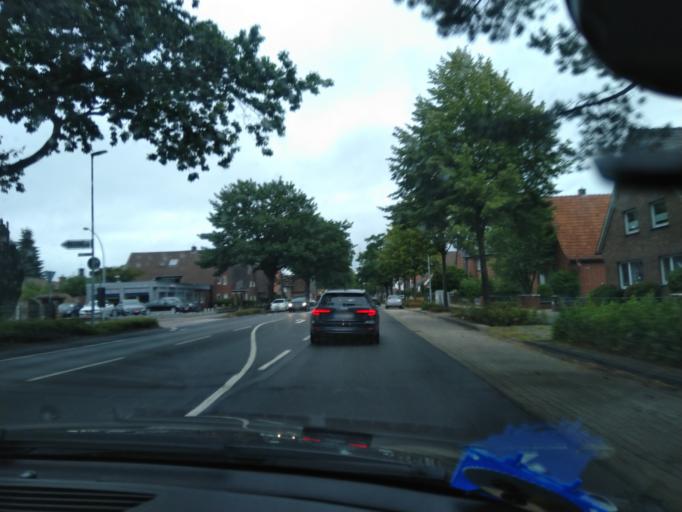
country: DE
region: Lower Saxony
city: Nordhorn
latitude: 52.4190
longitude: 7.0519
